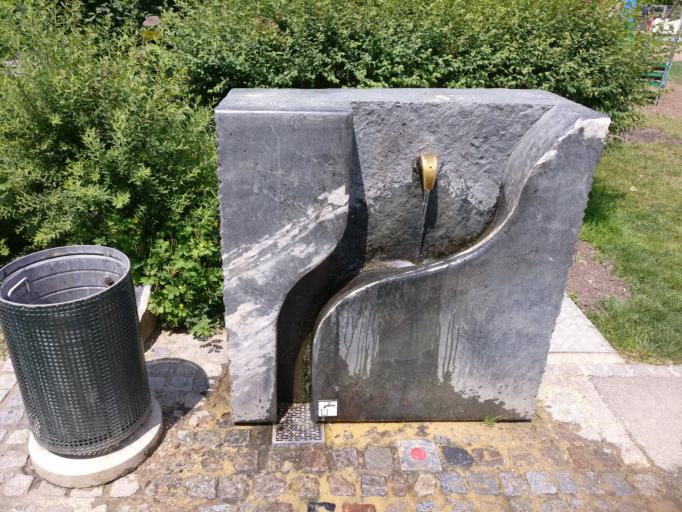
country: AT
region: Carinthia
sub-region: Klagenfurt am Woerthersee
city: Klagenfurt am Woerthersee
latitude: 46.6196
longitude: 14.2594
